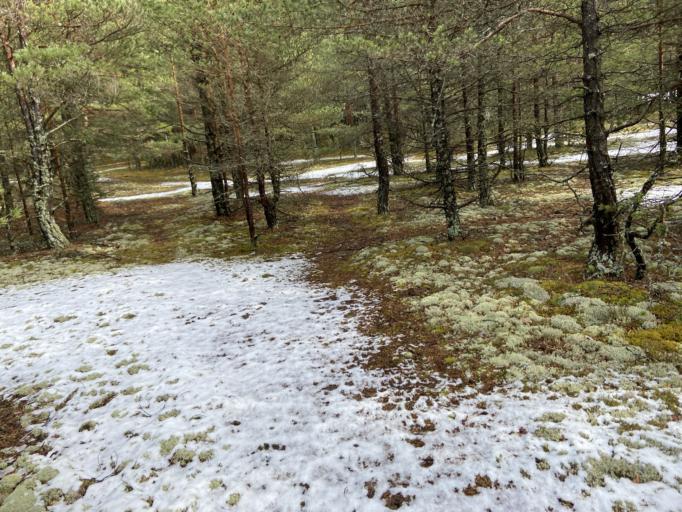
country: EE
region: Harju
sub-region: Loksa linn
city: Loksa
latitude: 59.6571
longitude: 25.6793
